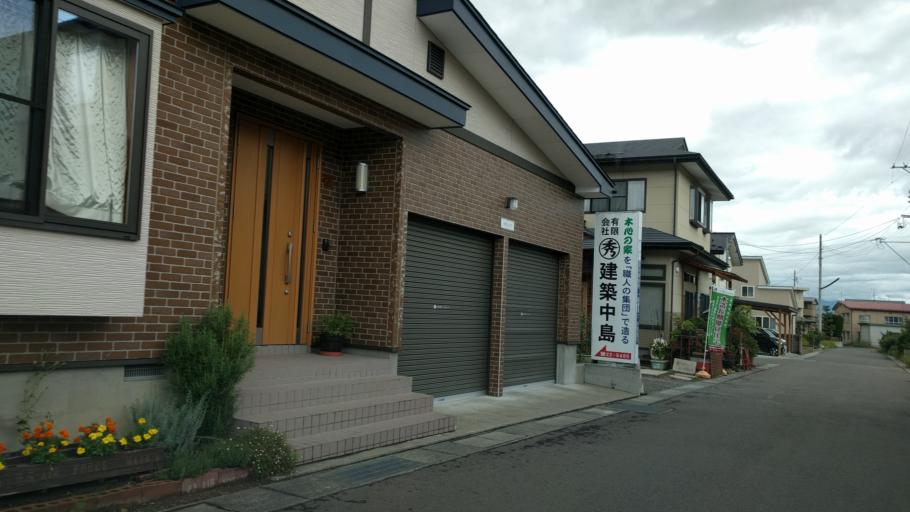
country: JP
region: Fukushima
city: Kitakata
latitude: 37.5108
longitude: 139.9382
